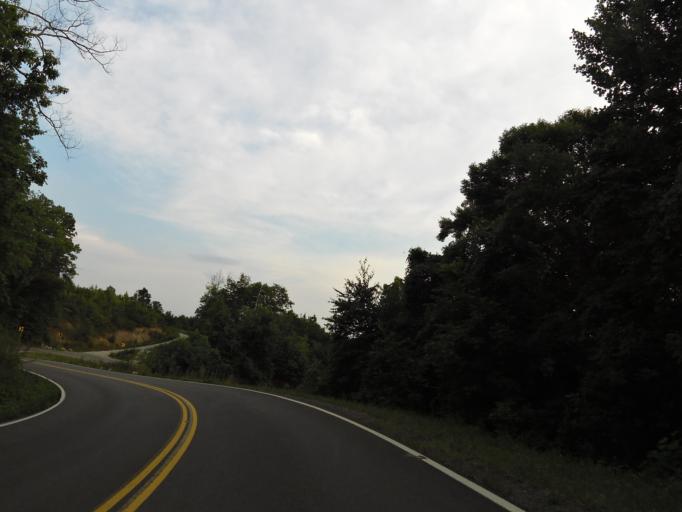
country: US
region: Tennessee
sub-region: Anderson County
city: Clinton
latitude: 36.1387
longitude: -84.2378
